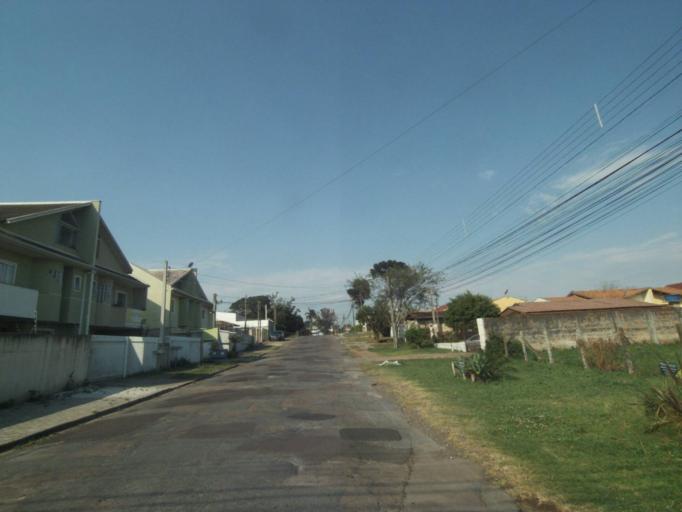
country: BR
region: Parana
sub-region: Sao Jose Dos Pinhais
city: Sao Jose dos Pinhais
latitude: -25.5080
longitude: -49.2562
